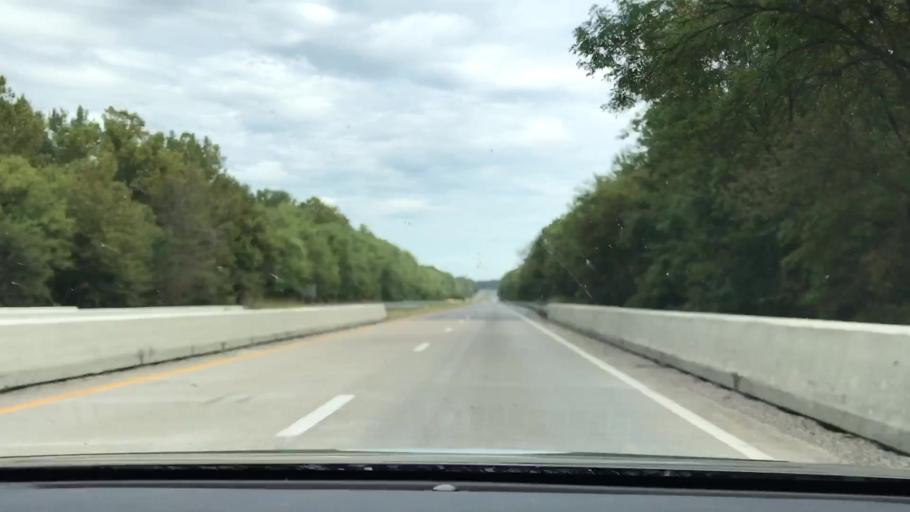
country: US
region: Kentucky
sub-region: Marshall County
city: Benton
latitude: 36.8786
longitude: -88.3591
